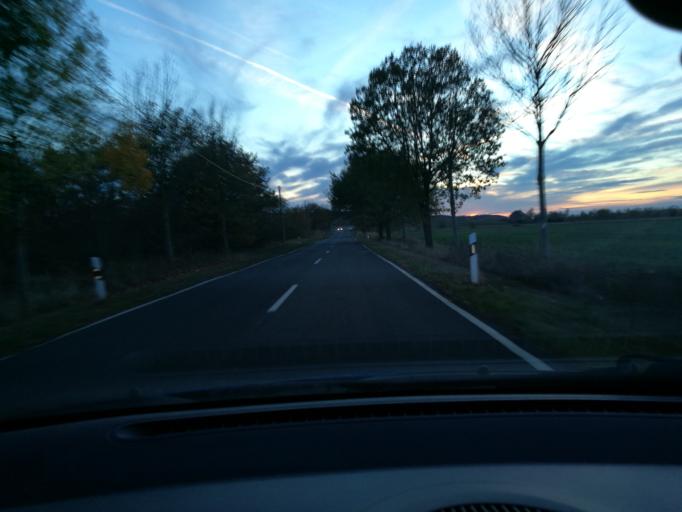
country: DE
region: Brandenburg
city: Lenzen
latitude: 53.0819
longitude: 11.4595
